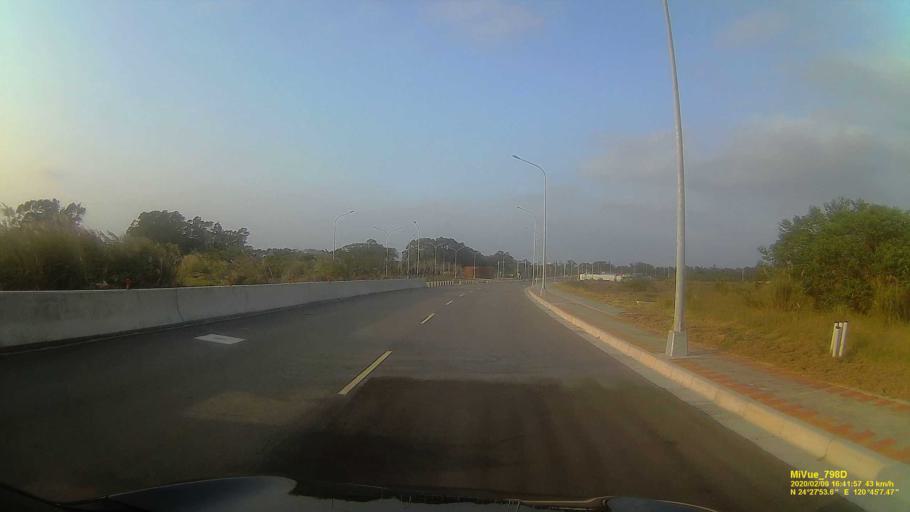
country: TW
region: Taiwan
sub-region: Miaoli
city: Miaoli
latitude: 24.4649
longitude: 120.7521
